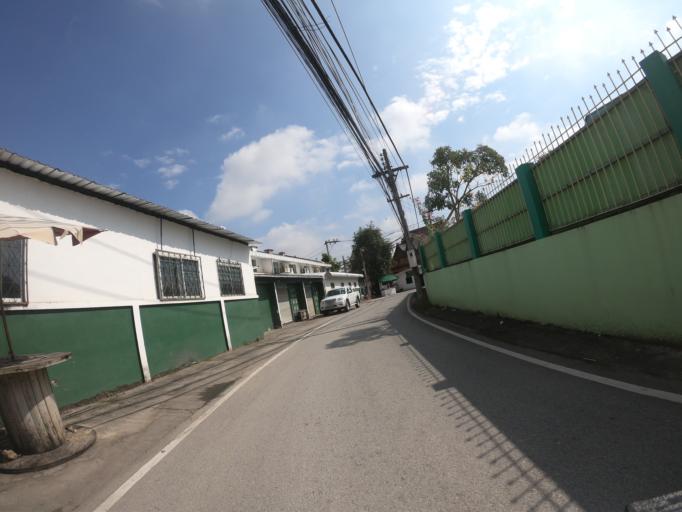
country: TH
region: Chiang Mai
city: Chiang Mai
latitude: 18.7469
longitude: 98.9596
